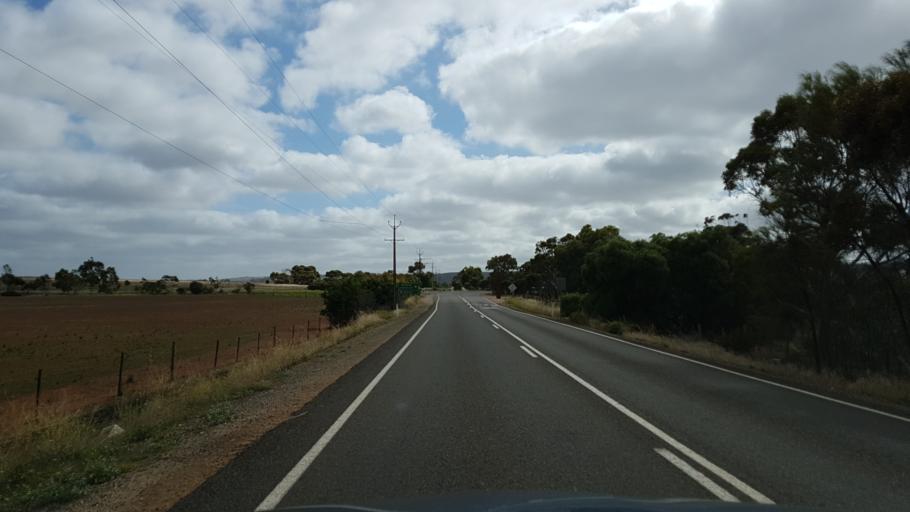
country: AU
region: South Australia
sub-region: Mount Barker
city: Callington
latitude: -35.1107
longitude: 139.0466
